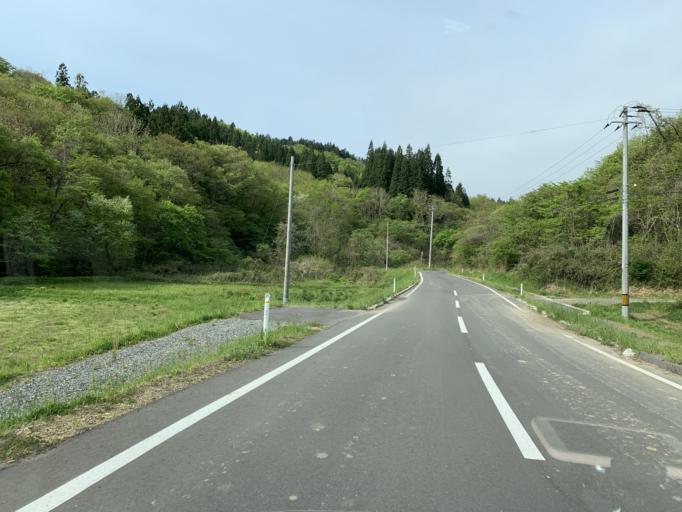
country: JP
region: Iwate
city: Ichinoseki
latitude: 38.9080
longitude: 141.0615
